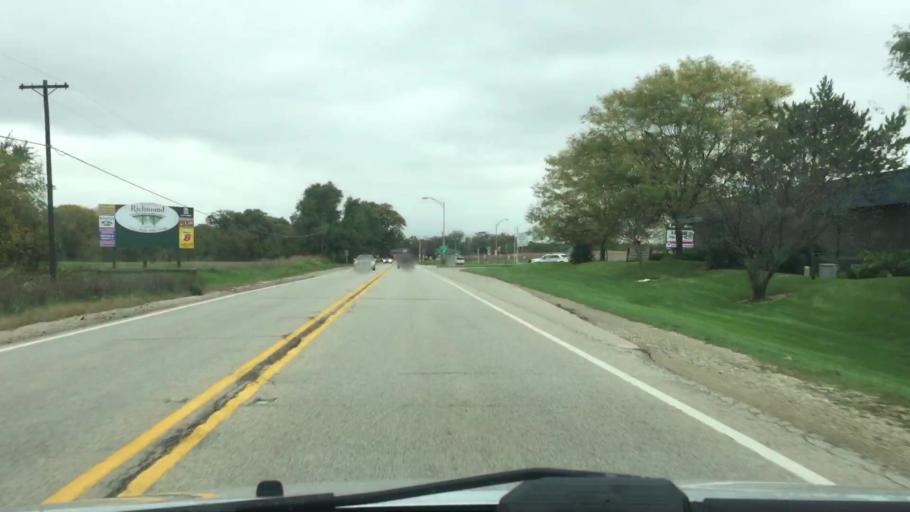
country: US
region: Illinois
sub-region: McHenry County
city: Richmond
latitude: 42.4934
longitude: -88.3102
